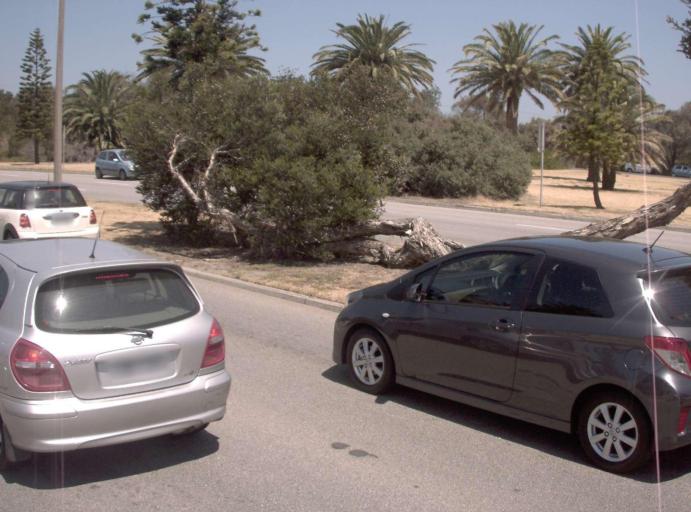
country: AU
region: Victoria
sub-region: Port Phillip
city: Elwood
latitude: -37.8811
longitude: 144.9778
